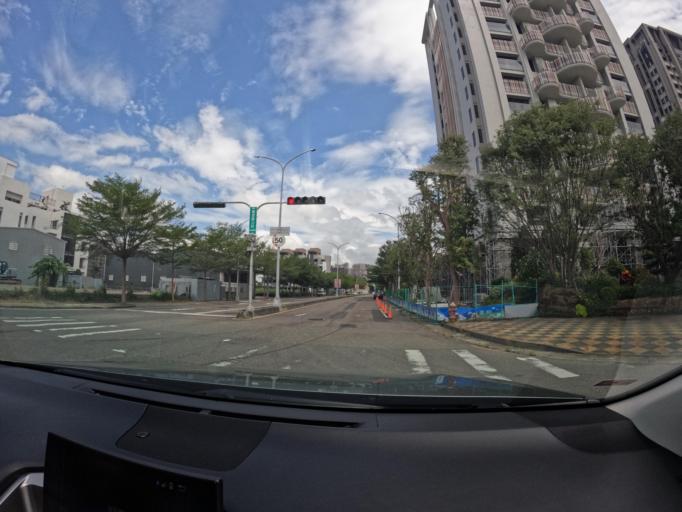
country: TW
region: Taiwan
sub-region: Taichung City
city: Taichung
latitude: 24.1361
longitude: 120.6263
